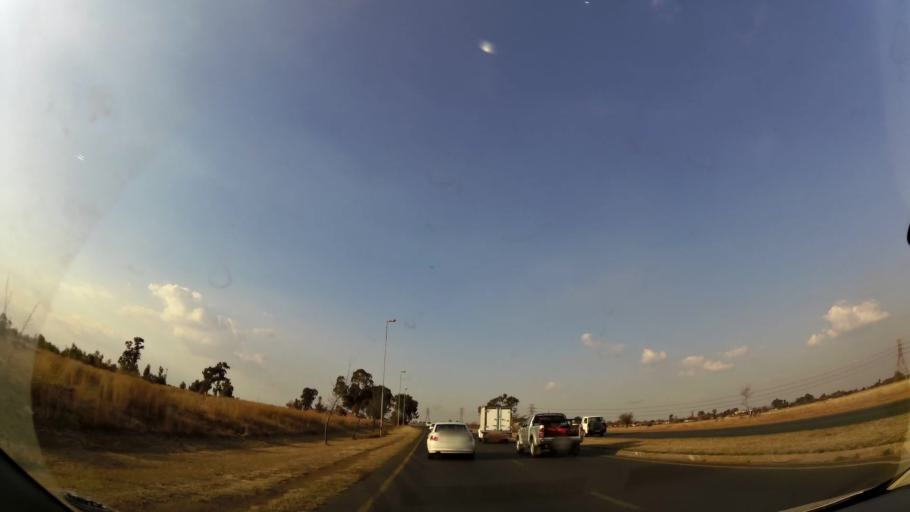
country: ZA
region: Gauteng
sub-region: Ekurhuleni Metropolitan Municipality
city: Germiston
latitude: -26.3387
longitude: 28.2258
